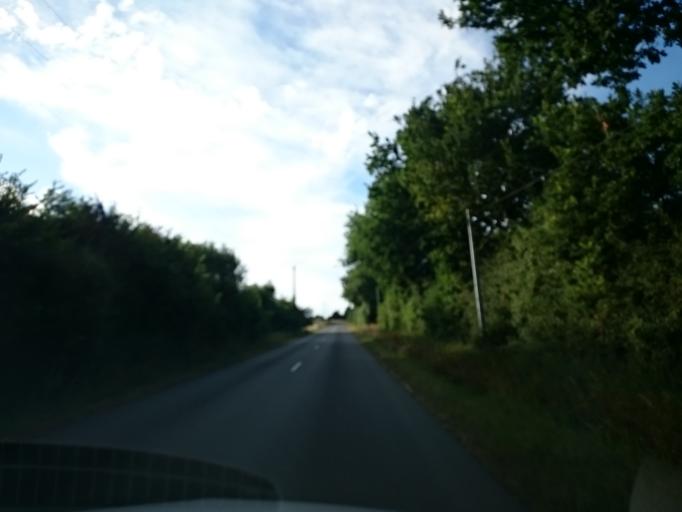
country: FR
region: Brittany
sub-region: Departement d'Ille-et-Vilaine
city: Pance
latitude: 47.8999
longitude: -1.6150
